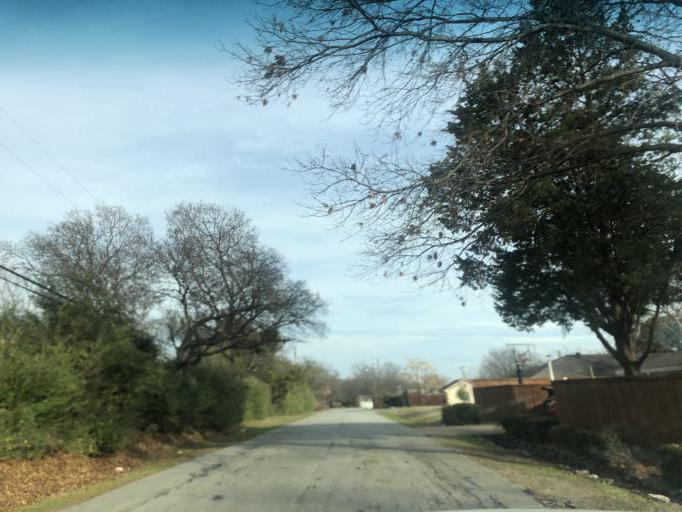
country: US
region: Texas
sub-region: Dallas County
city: Duncanville
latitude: 32.6692
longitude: -96.9029
